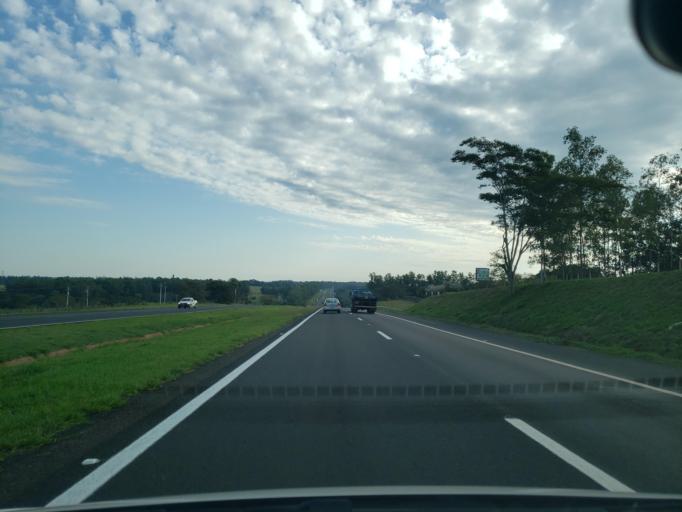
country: BR
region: Sao Paulo
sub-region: Guararapes
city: Guararapes
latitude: -21.2095
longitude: -50.6670
